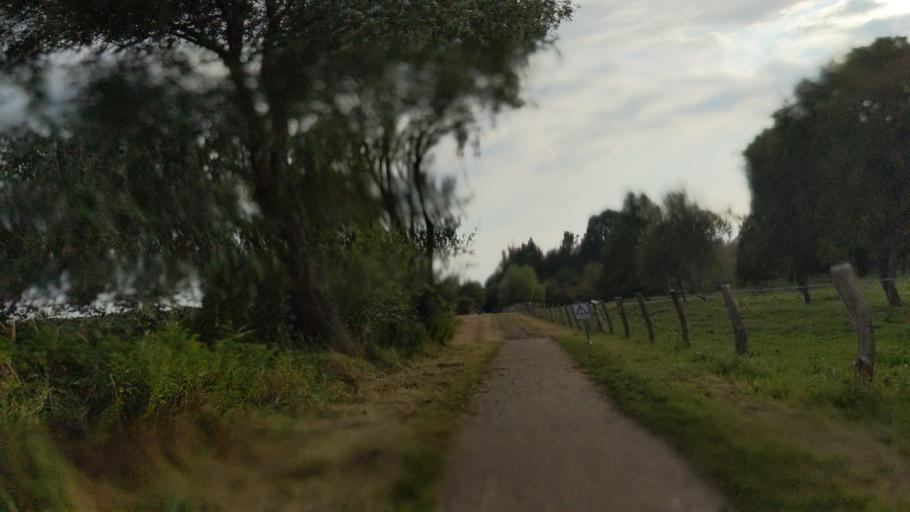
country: DE
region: Mecklenburg-Vorpommern
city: Dassow
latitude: 53.9727
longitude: 10.9514
